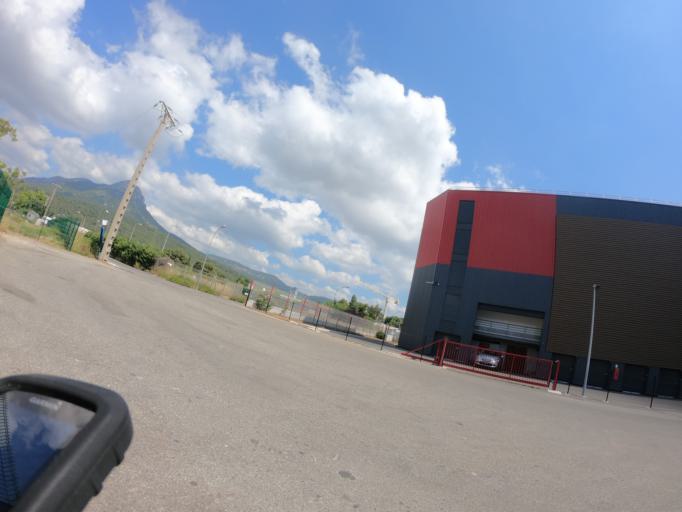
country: FR
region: Provence-Alpes-Cote d'Azur
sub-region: Departement du Var
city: La Farlede
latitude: 43.1405
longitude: 6.0328
